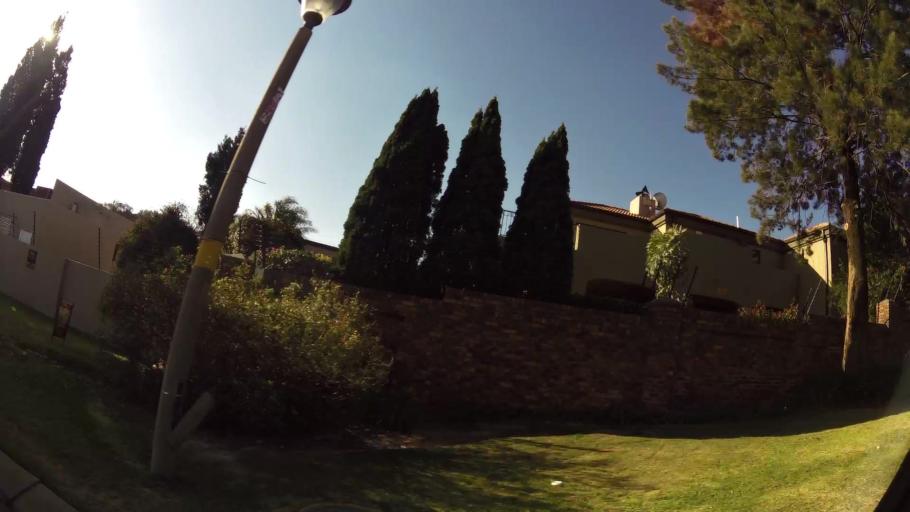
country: ZA
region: Gauteng
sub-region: City of Johannesburg Metropolitan Municipality
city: Johannesburg
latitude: -26.2804
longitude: 28.0725
